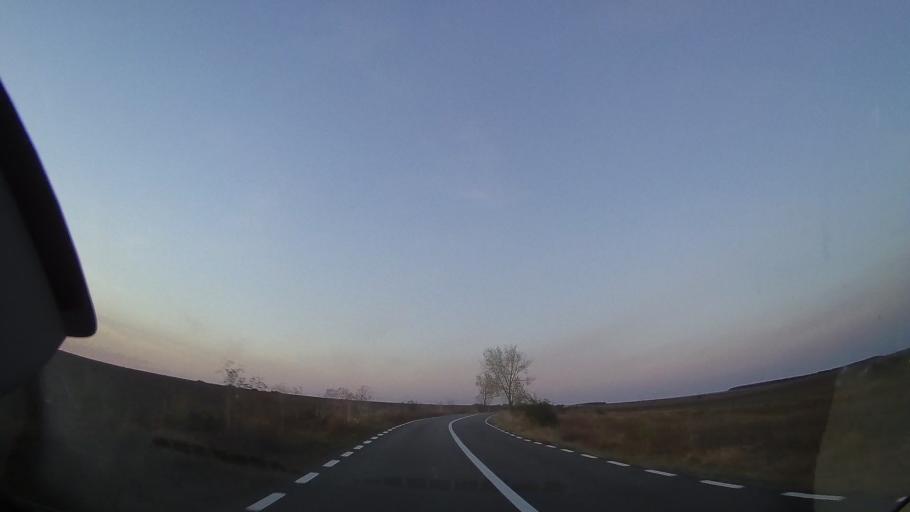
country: RO
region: Constanta
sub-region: Comuna Cobadin
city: Cobadin
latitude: 44.0271
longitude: 28.2632
